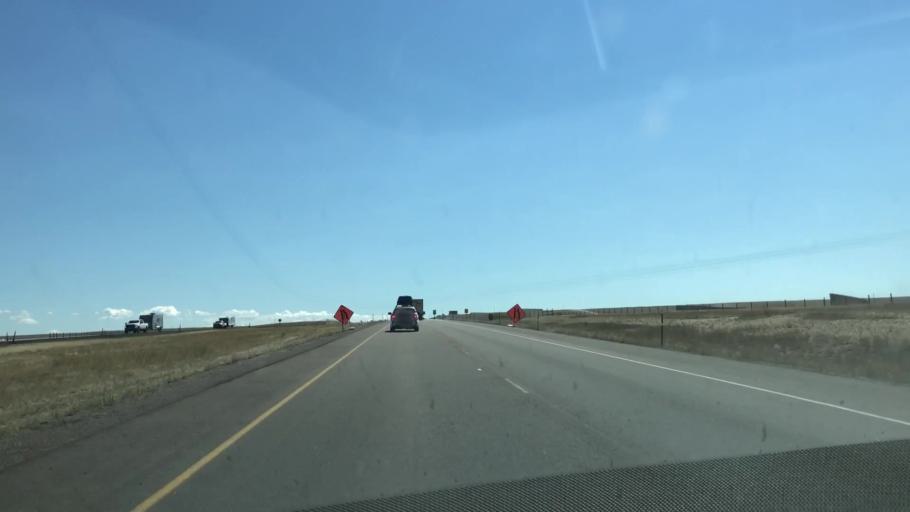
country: US
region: Wyoming
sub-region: Albany County
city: Laramie
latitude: 41.5476
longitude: -106.0884
